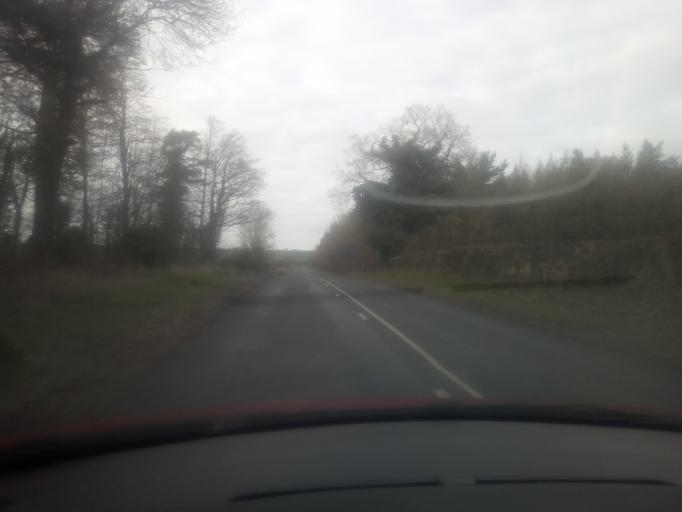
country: GB
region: England
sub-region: Darlington
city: Summerhouse
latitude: 54.5752
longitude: -1.6777
